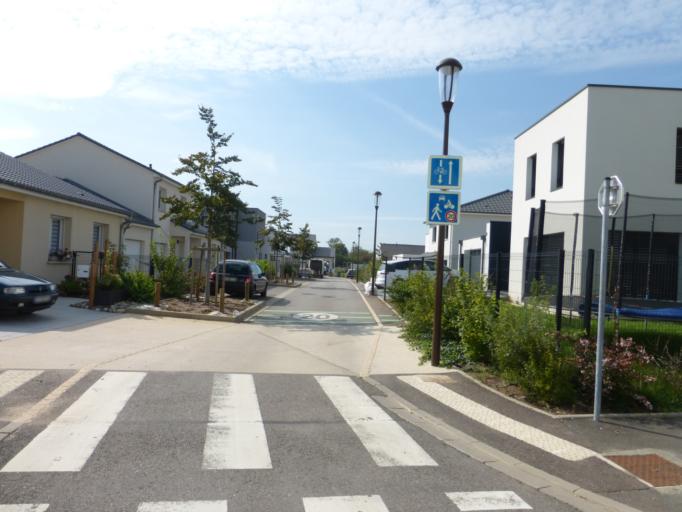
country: FR
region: Lorraine
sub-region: Departement de Meurthe-et-Moselle
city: Pulnoy
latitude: 48.7020
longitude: 6.2505
